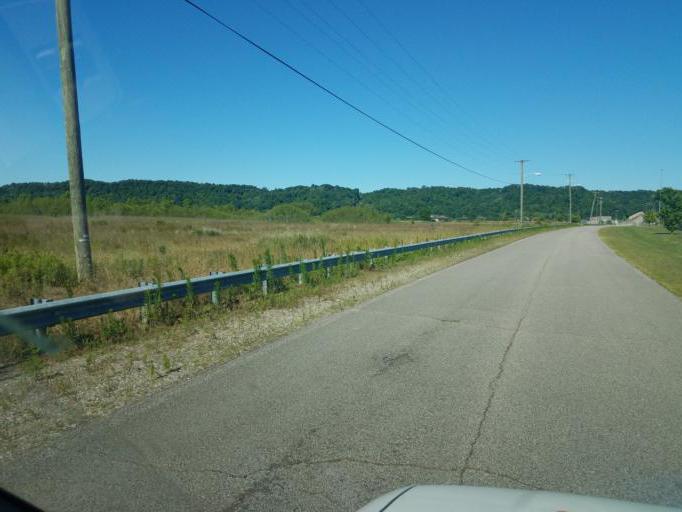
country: US
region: Ohio
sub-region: Gallia County
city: Gallipolis
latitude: 38.6812
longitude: -82.1777
